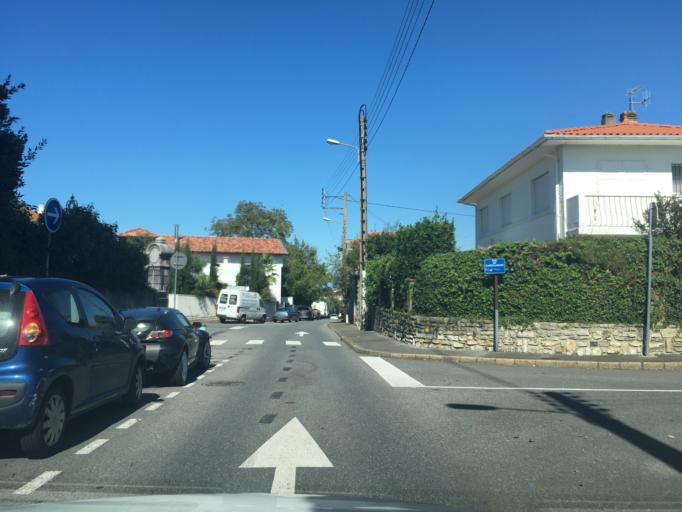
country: FR
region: Aquitaine
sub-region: Departement des Pyrenees-Atlantiques
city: Biarritz
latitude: 43.4805
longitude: -1.5520
